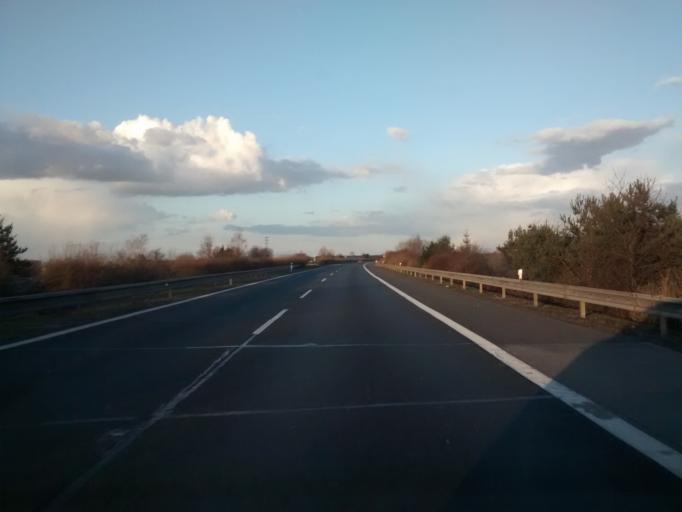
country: CZ
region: Central Bohemia
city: Sestajovice
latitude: 50.1186
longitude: 14.6726
